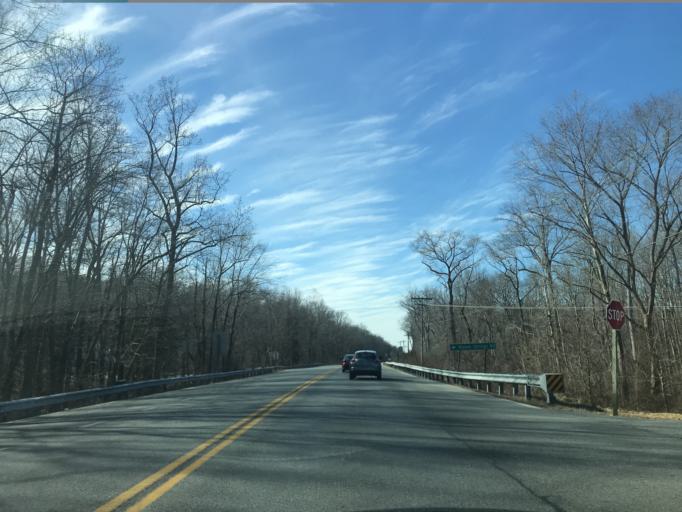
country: US
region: Maryland
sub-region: Charles County
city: Potomac Heights
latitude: 38.5838
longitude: -77.1202
